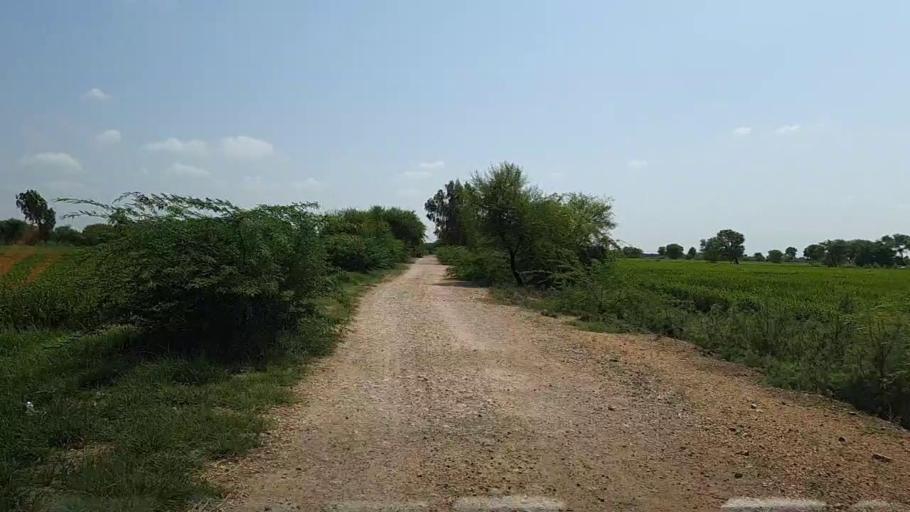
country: PK
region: Sindh
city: Kario
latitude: 24.7032
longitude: 68.6157
